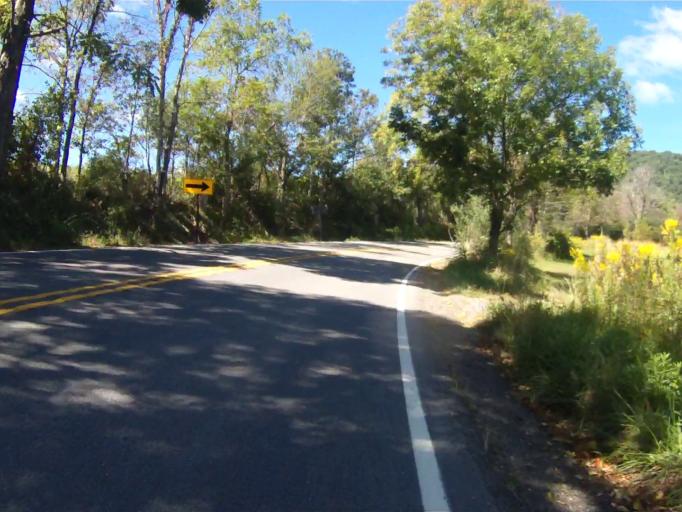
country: US
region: Pennsylvania
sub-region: Centre County
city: Park Forest Village
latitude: 40.9265
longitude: -77.9245
